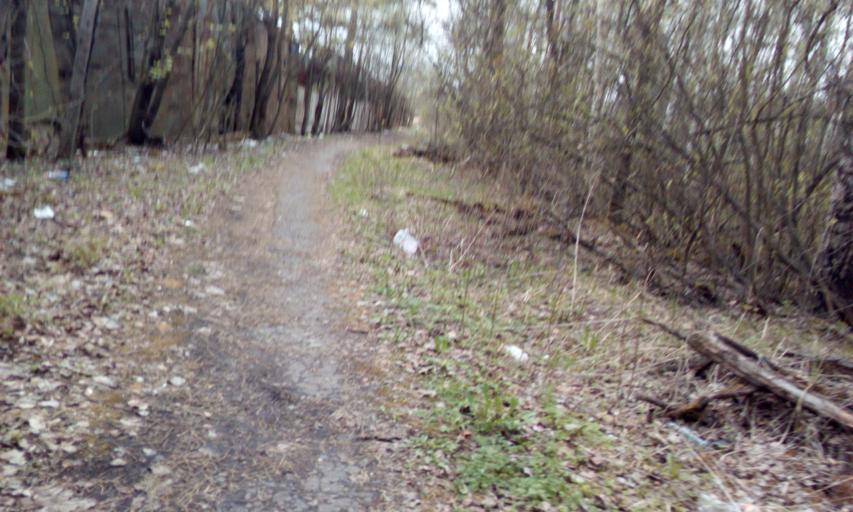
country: RU
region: Moscow
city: Vnukovo
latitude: 55.6089
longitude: 37.1935
